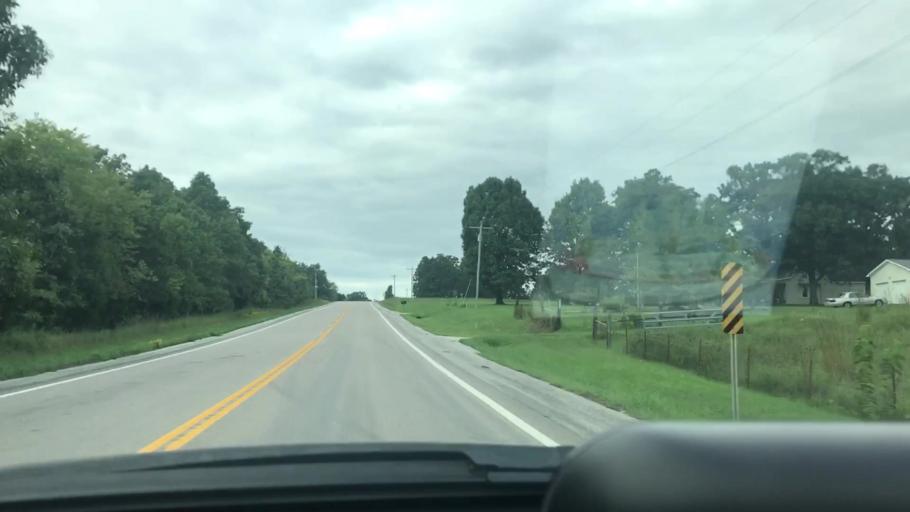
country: US
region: Missouri
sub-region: Benton County
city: Warsaw
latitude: 38.1511
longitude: -93.2942
